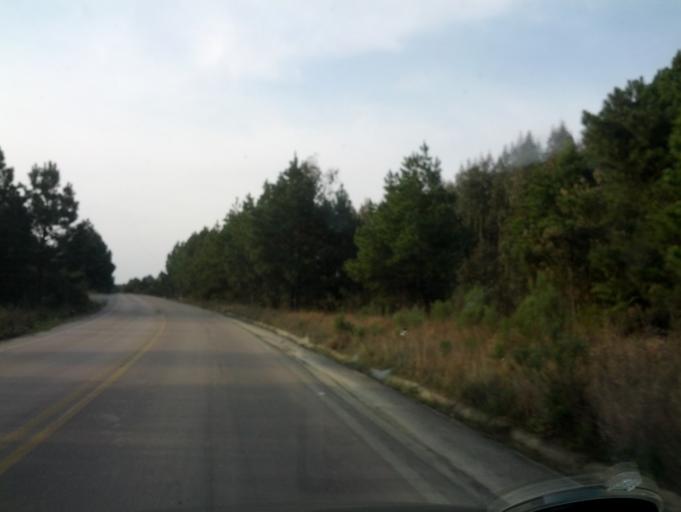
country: BR
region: Santa Catarina
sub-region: Otacilio Costa
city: Otacilio Costa
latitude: -27.4320
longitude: -50.1219
